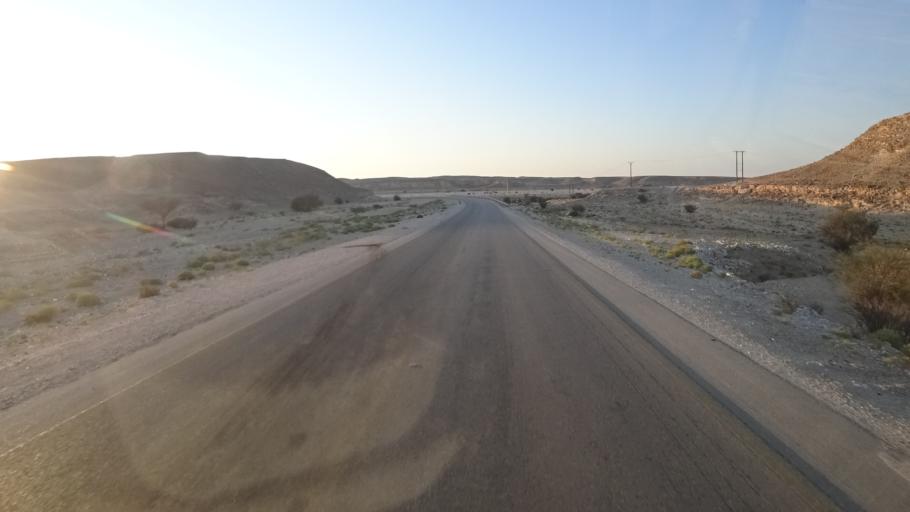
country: OM
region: Zufar
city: Salalah
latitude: 17.5317
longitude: 53.3881
